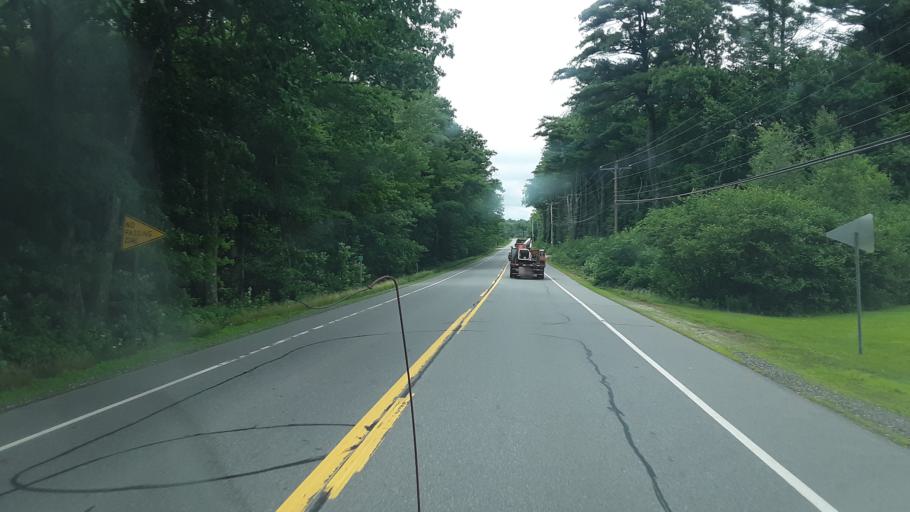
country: US
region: New Hampshire
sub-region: Rockingham County
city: Nottingham
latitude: 43.1736
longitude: -71.0952
